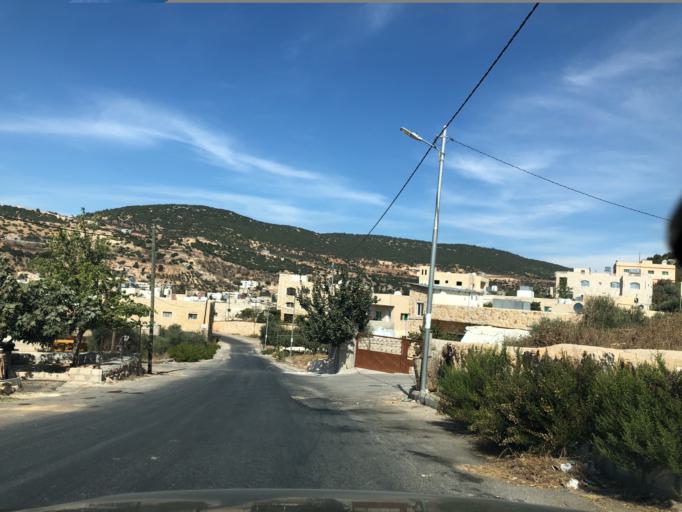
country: JO
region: Irbid
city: `Ayn Jannah
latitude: 32.3290
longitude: 35.7607
